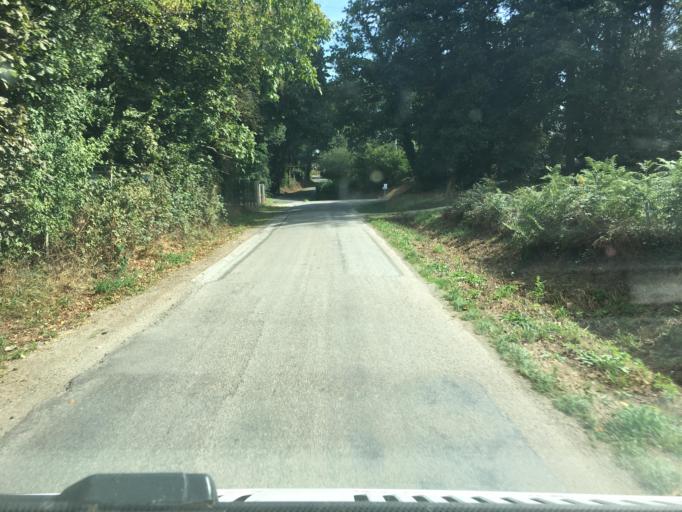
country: FR
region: Brittany
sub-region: Departement des Cotes-d'Armor
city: Mur-de-Bretagne
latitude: 48.2056
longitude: -3.0040
